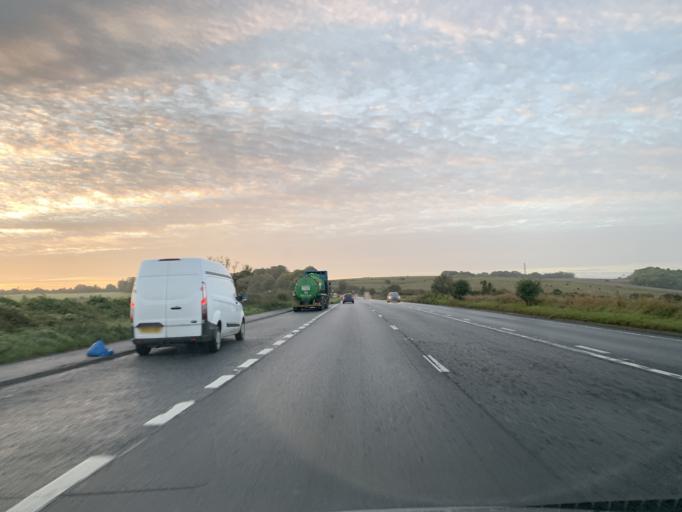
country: GB
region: England
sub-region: Wiltshire
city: Alderbury
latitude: 51.0264
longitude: -1.7108
